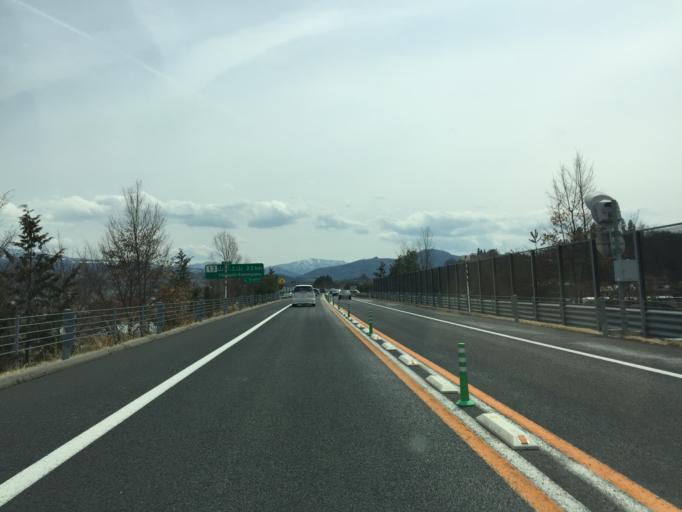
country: JP
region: Yamagata
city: Kaminoyama
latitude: 38.2067
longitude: 140.2942
